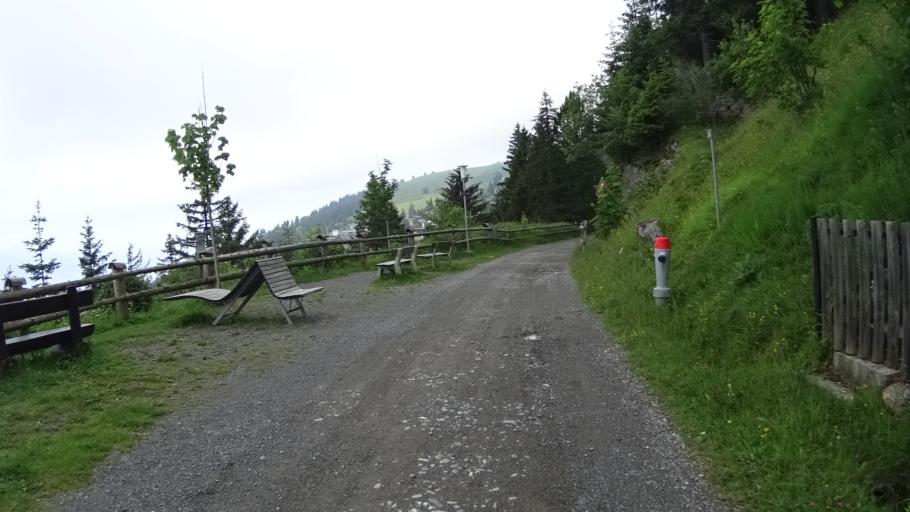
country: CH
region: Lucerne
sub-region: Lucerne-Land District
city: Vitznau
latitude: 47.0414
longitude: 8.4763
